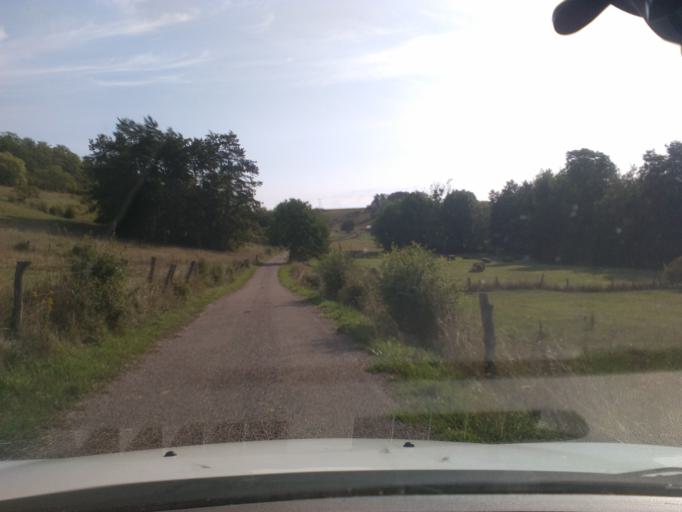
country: FR
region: Lorraine
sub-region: Departement des Vosges
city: Mirecourt
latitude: 48.3120
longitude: 6.0884
